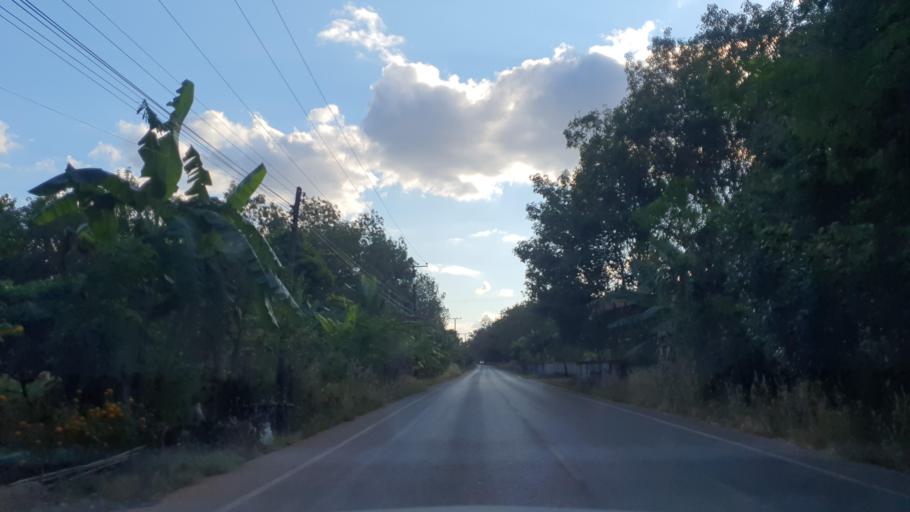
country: TH
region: Changwat Bueng Kan
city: Si Wilai
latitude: 18.1387
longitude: 103.8885
